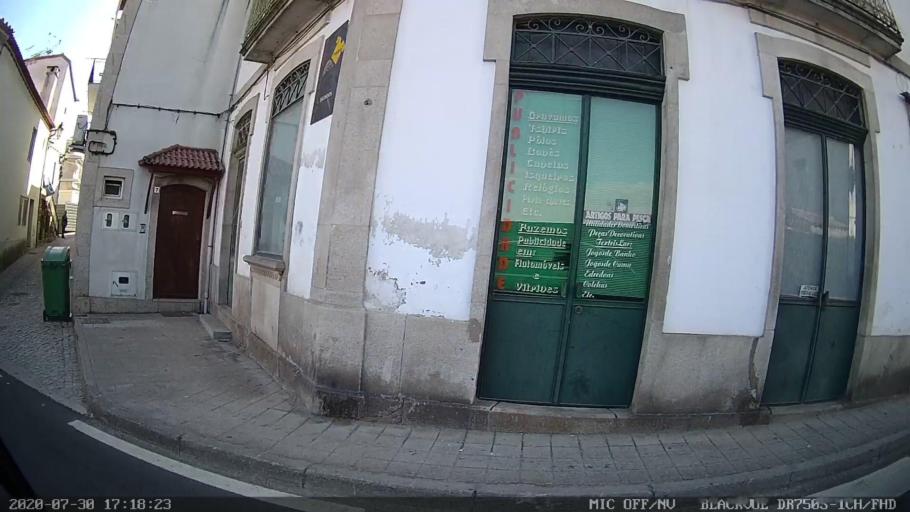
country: PT
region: Vila Real
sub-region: Sabrosa
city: Sabrosa
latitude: 41.2774
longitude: -7.4749
